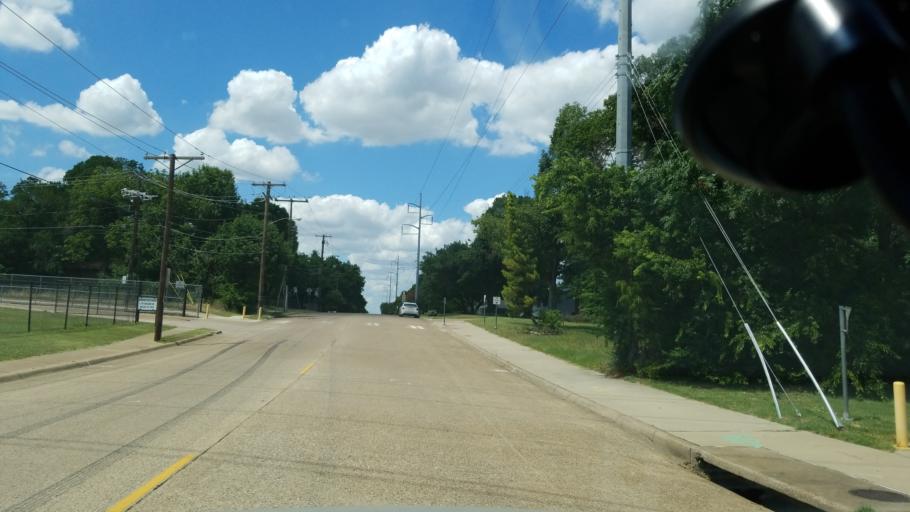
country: US
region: Texas
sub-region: Dallas County
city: Cockrell Hill
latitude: 32.6995
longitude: -96.8743
